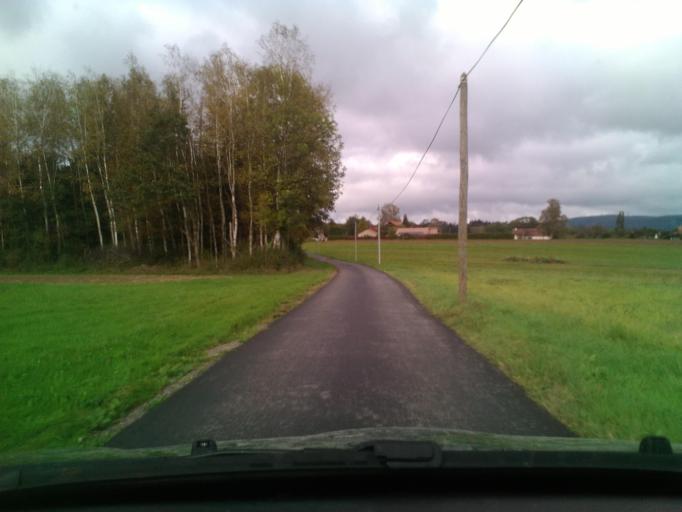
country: FR
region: Lorraine
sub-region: Departement des Vosges
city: Saint-Michel-sur-Meurthe
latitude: 48.3306
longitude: 6.8724
